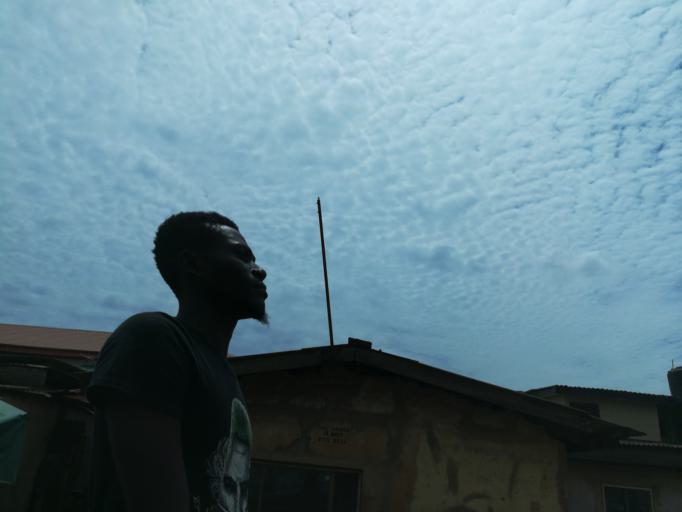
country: NG
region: Lagos
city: Oshodi
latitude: 6.5619
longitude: 3.3302
